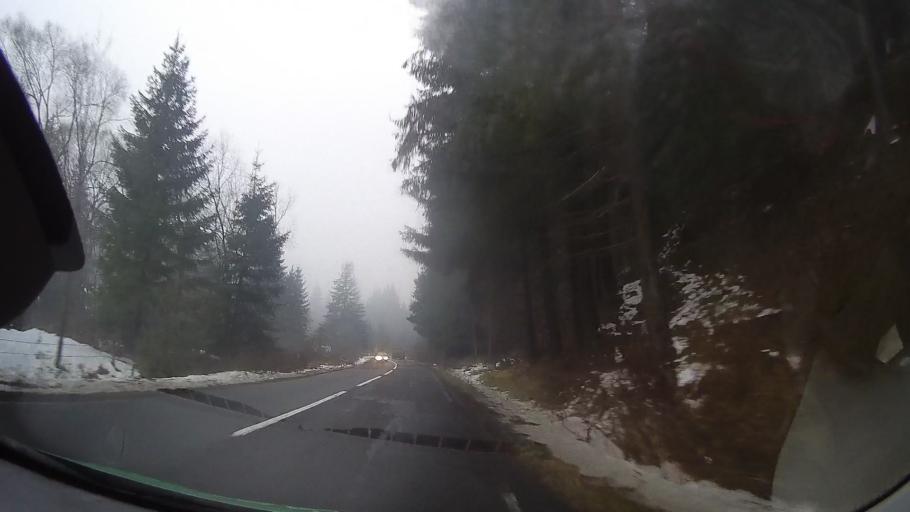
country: RO
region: Harghita
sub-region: Municipiul Gheorgheni
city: Gheorgheni
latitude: 46.7497
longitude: 25.6853
